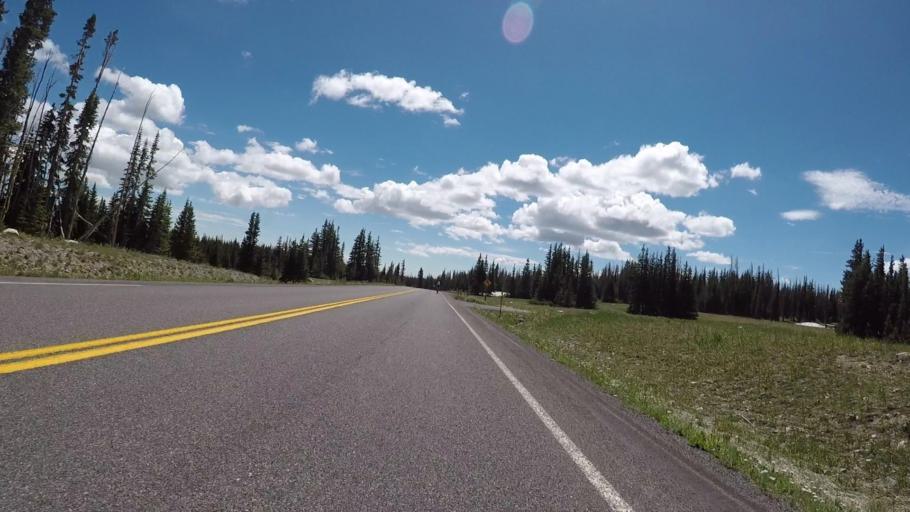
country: US
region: Wyoming
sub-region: Carbon County
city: Saratoga
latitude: 41.3517
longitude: -106.2605
